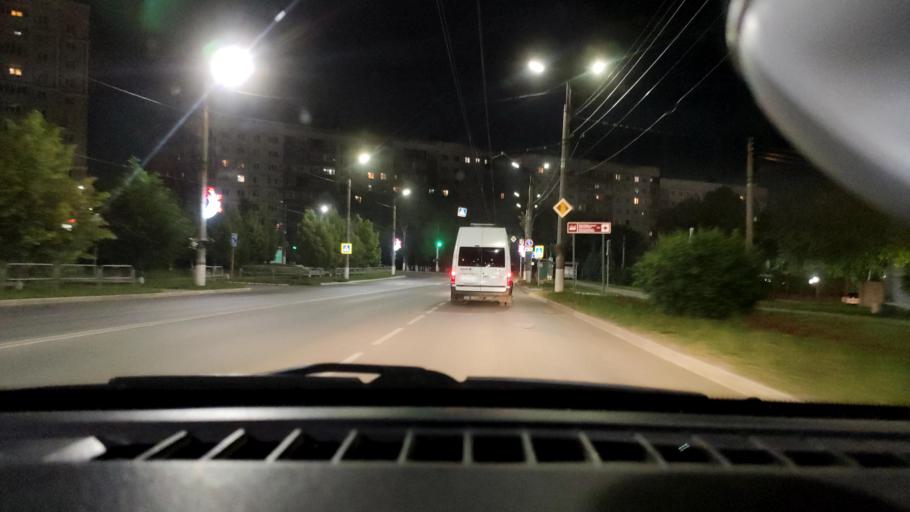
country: RU
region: Samara
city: Novokuybyshevsk
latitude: 53.1029
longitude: 49.9554
